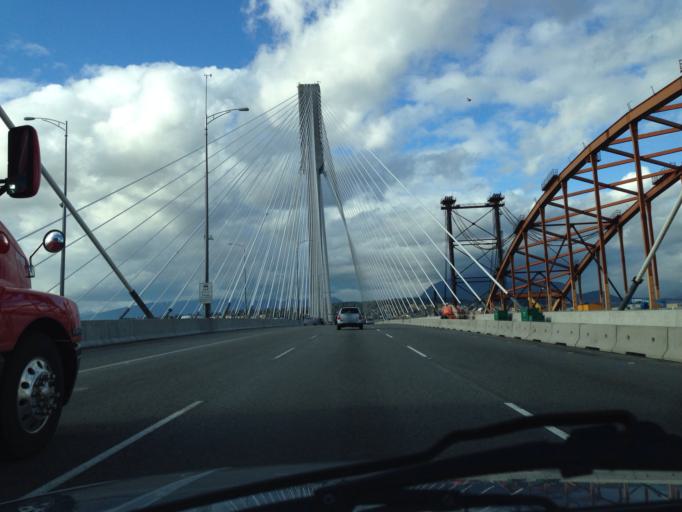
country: CA
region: British Columbia
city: Port Moody
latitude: 49.2172
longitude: -122.8119
